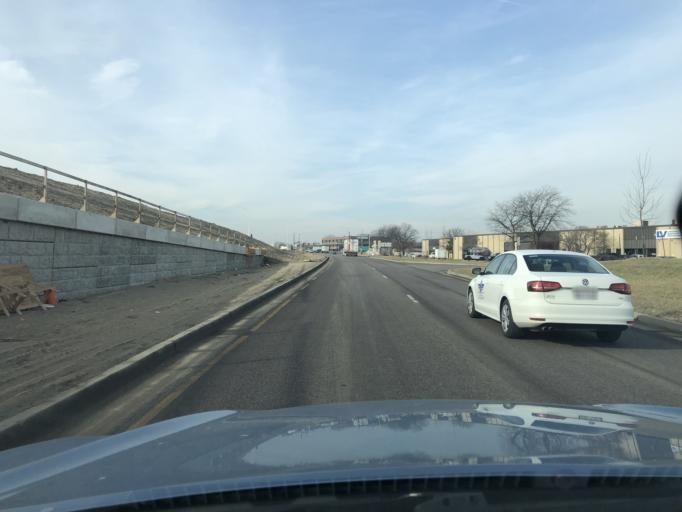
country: US
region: Illinois
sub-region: Cook County
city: Elk Grove Village
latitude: 41.9827
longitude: -87.9550
